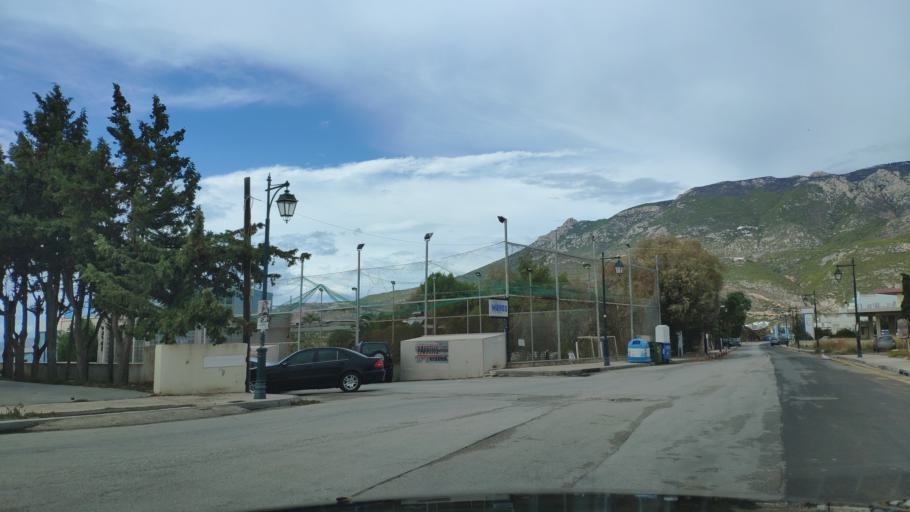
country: GR
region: Peloponnese
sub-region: Nomos Korinthias
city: Loutraki
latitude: 37.9618
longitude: 22.9702
